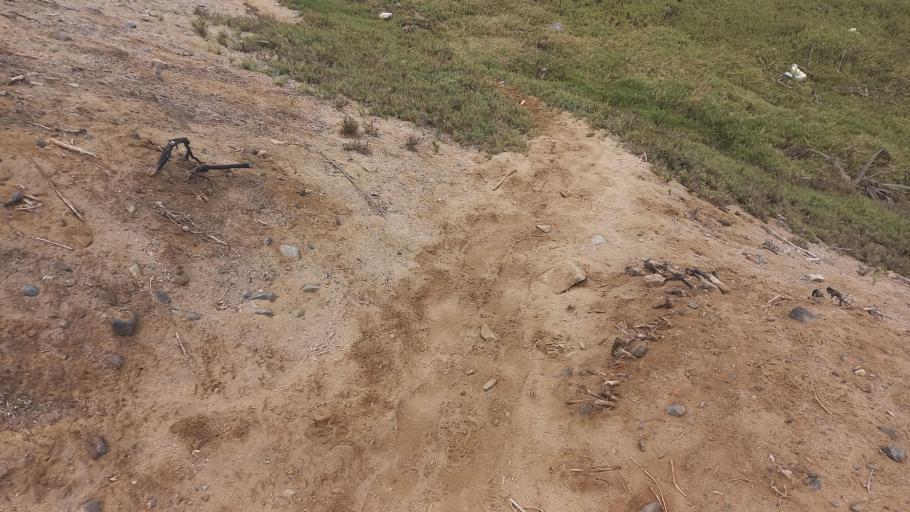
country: PE
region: La Libertad
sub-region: Provincia de Trujillo
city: Huanchaco
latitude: -8.1120
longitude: -79.0819
